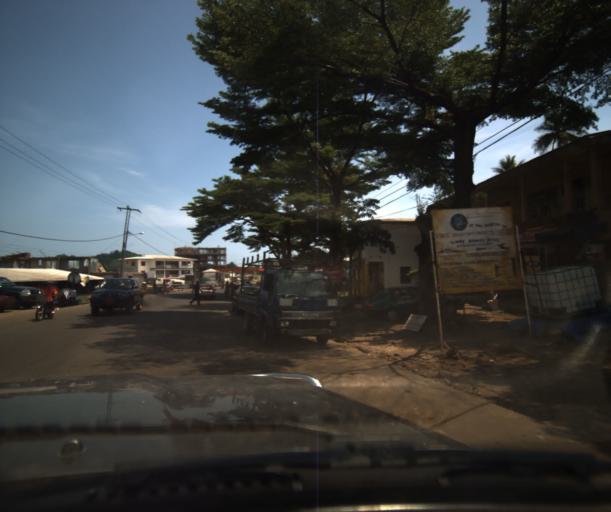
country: CM
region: South-West Province
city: Limbe
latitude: 4.0168
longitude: 9.2084
